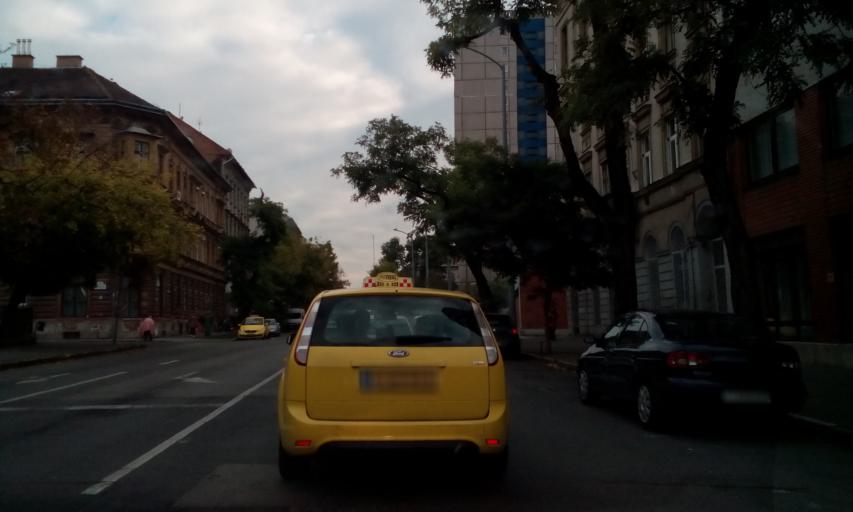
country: HU
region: Budapest
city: Budapest VIII. keruelet
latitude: 47.4886
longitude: 19.0846
